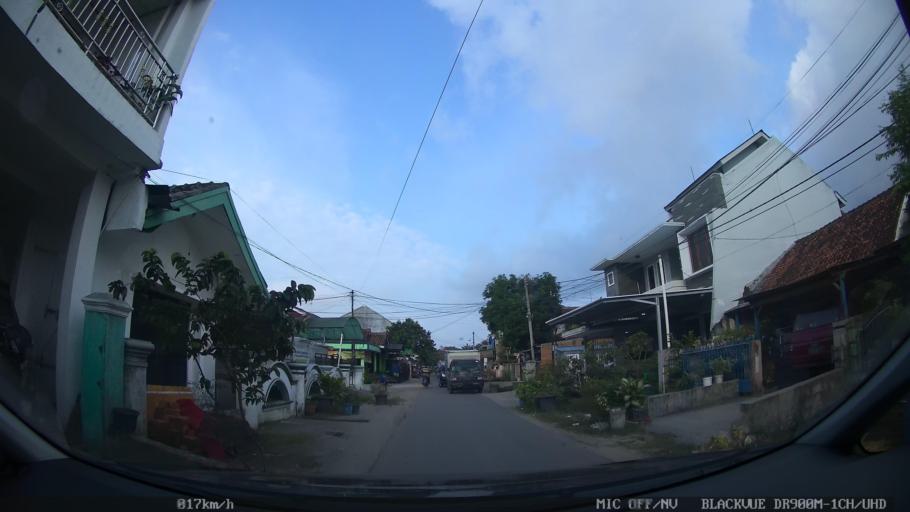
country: ID
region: Lampung
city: Kedaton
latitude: -5.4034
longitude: 105.3067
